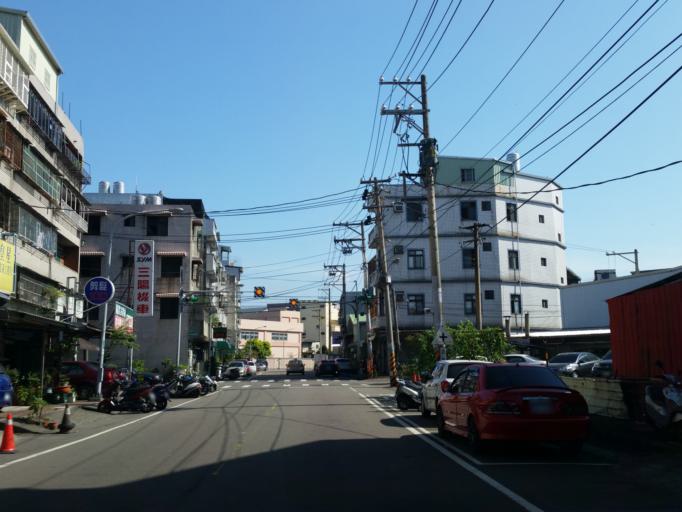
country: TW
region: Taiwan
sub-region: Taoyuan
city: Taoyuan
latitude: 24.9879
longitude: 121.3200
